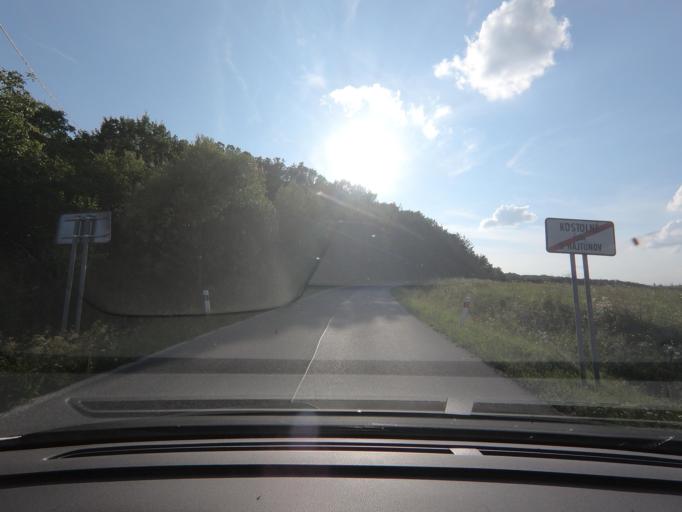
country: SK
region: Nitriansky
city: Stara Tura
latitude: 48.7268
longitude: 17.6801
